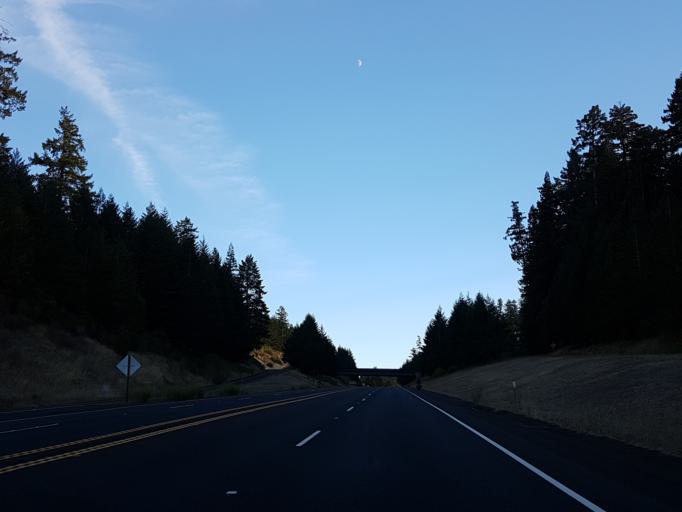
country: US
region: California
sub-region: Humboldt County
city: Redway
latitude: 39.9471
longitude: -123.7806
